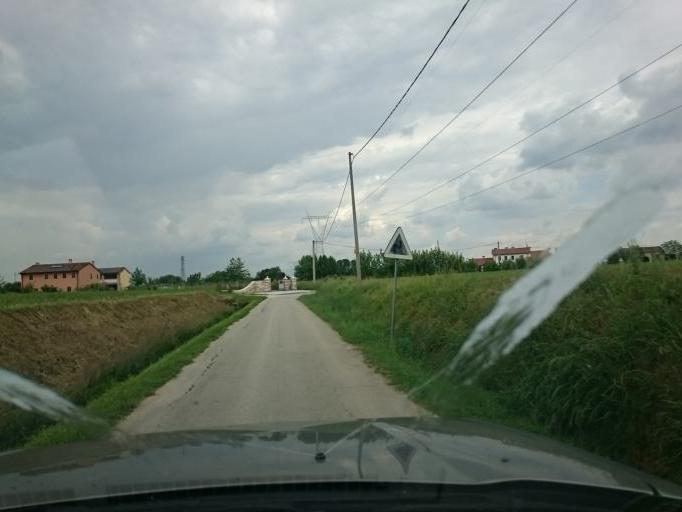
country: IT
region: Veneto
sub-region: Provincia di Vicenza
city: Villaganzerla
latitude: 45.4525
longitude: 11.6413
